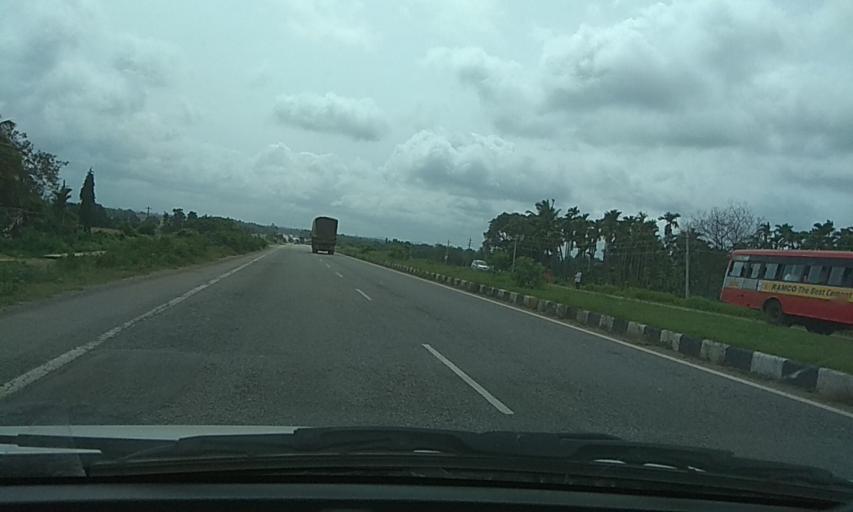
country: IN
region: Karnataka
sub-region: Davanagere
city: Mayakonda
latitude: 14.4056
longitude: 75.9990
